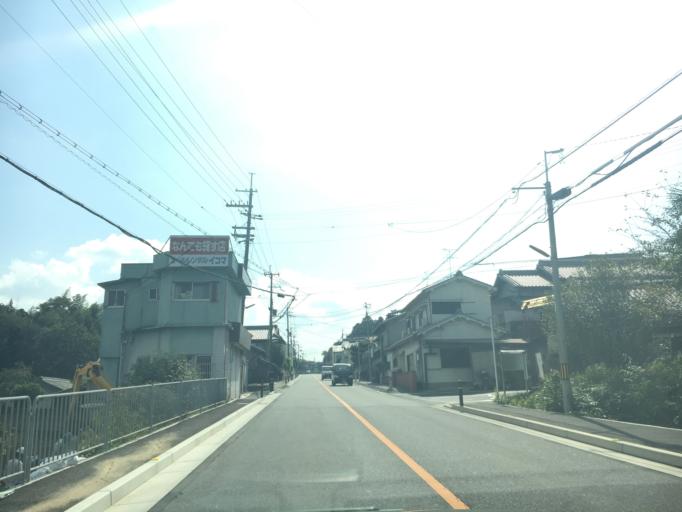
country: JP
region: Nara
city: Nara-shi
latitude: 34.7236
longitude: 135.8240
